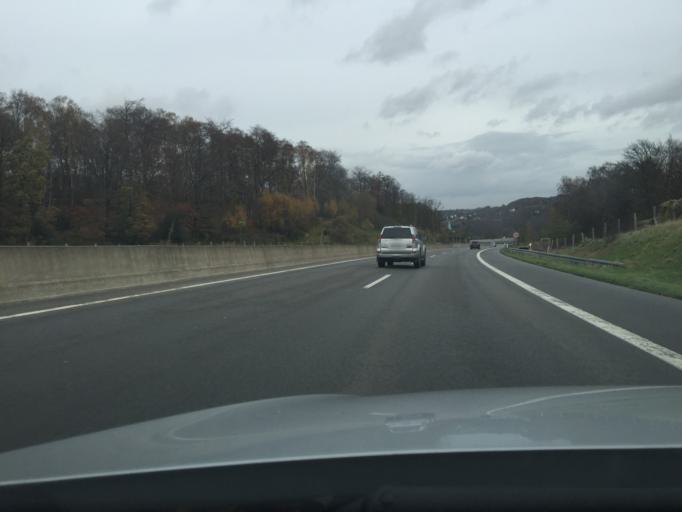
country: DE
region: North Rhine-Westphalia
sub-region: Regierungsbezirk Dusseldorf
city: Velbert
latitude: 51.3729
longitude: 7.0724
